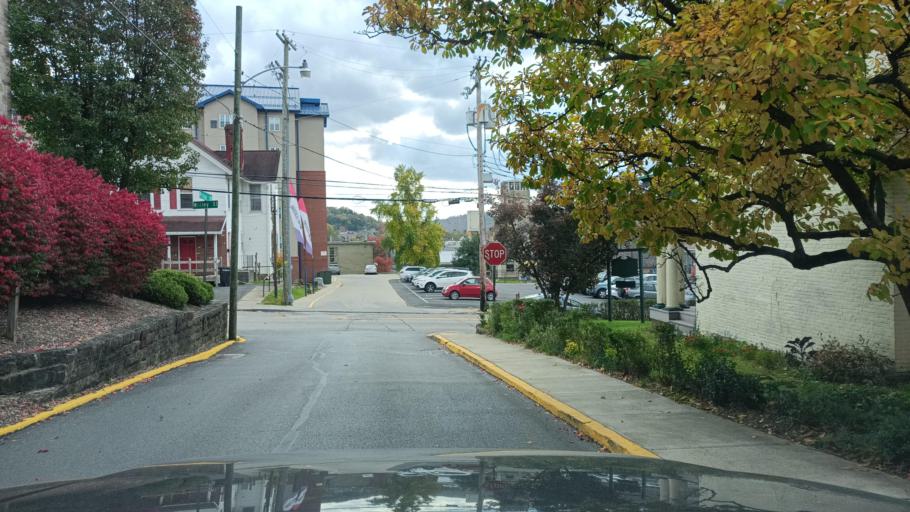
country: US
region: West Virginia
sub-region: Monongalia County
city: Morgantown
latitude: 39.6317
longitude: -79.9519
